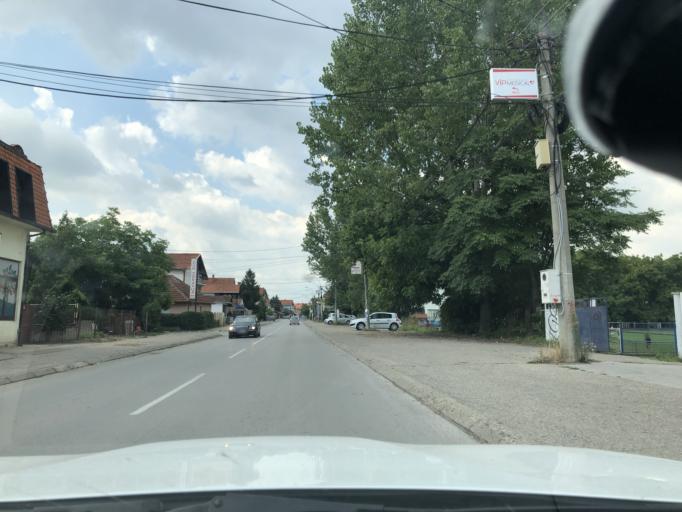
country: RS
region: Central Serbia
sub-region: Jablanicki Okrug
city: Leskovac
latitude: 42.9929
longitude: 21.9318
